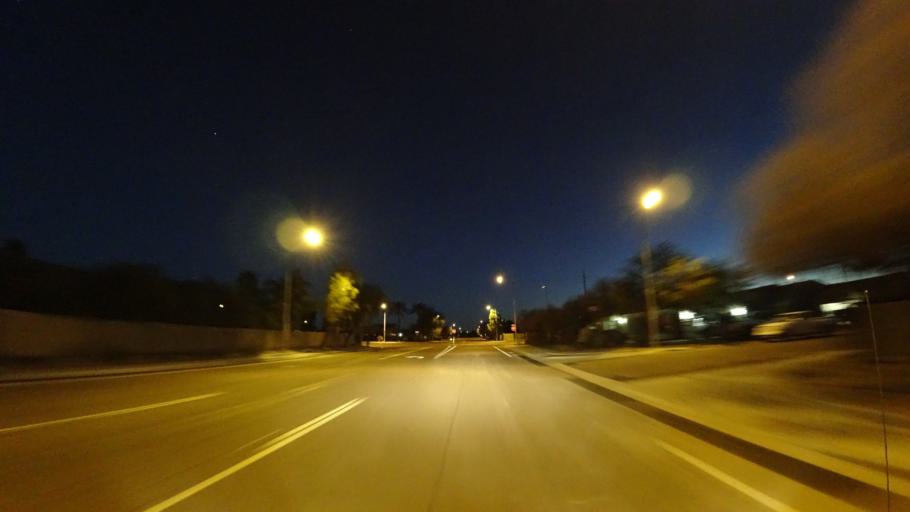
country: US
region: Arizona
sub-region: Maricopa County
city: Chandler
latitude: 33.2922
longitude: -111.8677
